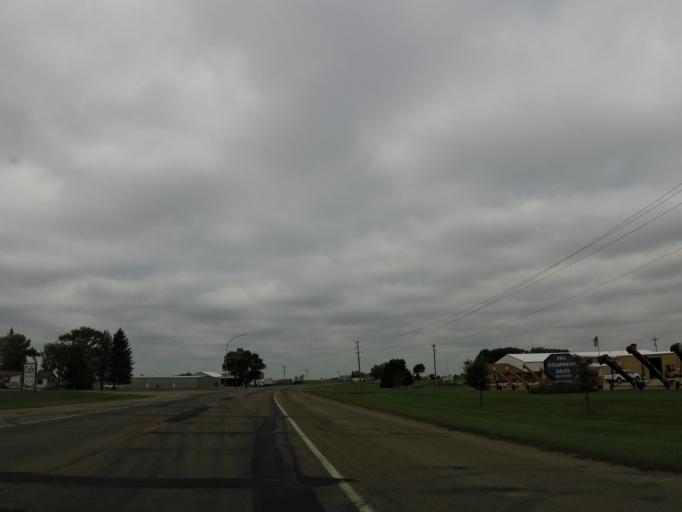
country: US
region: Minnesota
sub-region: Renville County
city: Olivia
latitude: 44.7781
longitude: -95.0249
